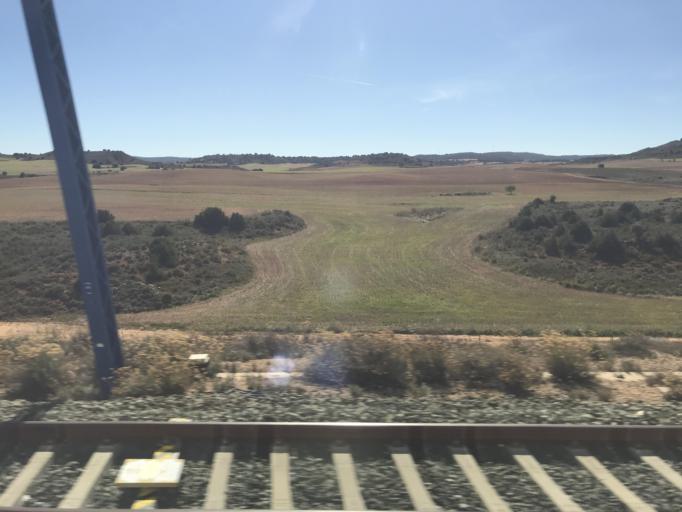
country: ES
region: Aragon
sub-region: Provincia de Zaragoza
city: Cabolafuente
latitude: 41.2250
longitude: -2.0768
